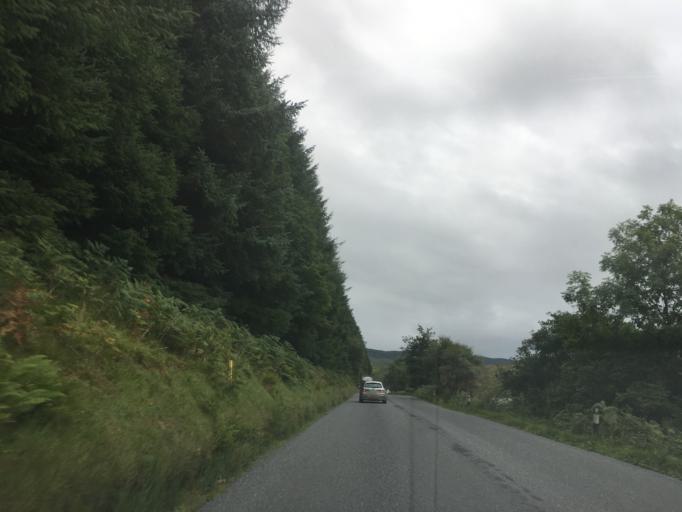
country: GB
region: Scotland
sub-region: Argyll and Bute
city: Oban
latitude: 56.2724
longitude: -5.4782
